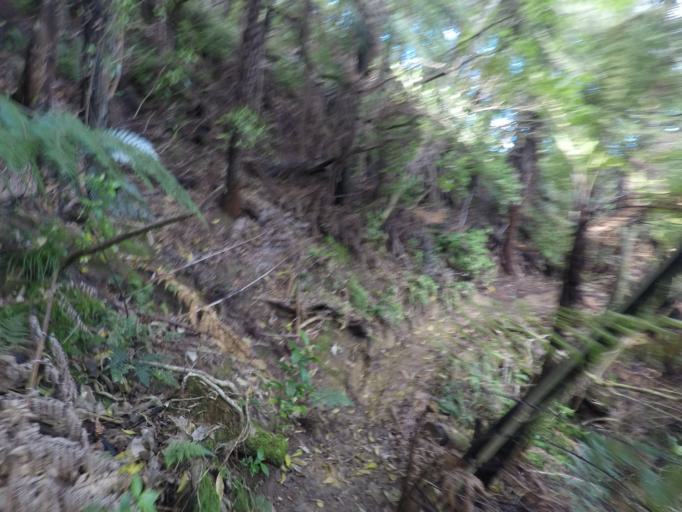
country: NZ
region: Auckland
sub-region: Auckland
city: Rothesay Bay
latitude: -36.7381
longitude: 174.7149
